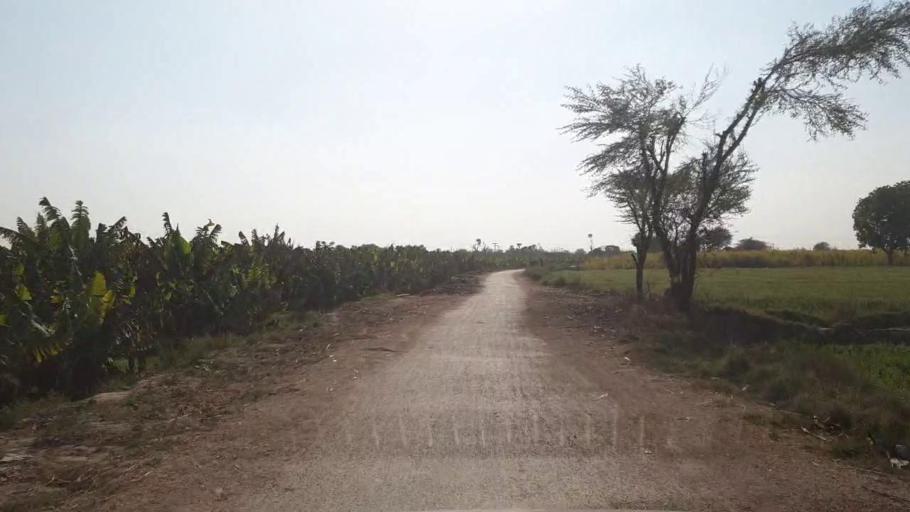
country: PK
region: Sindh
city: Chambar
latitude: 25.3388
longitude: 68.7516
